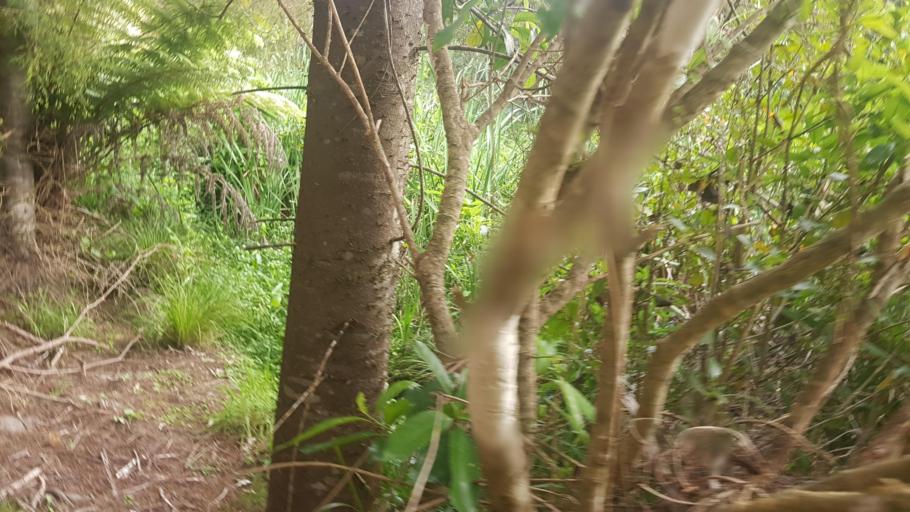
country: NZ
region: Auckland
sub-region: Auckland
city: Pakuranga
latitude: -36.7801
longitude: 175.0001
